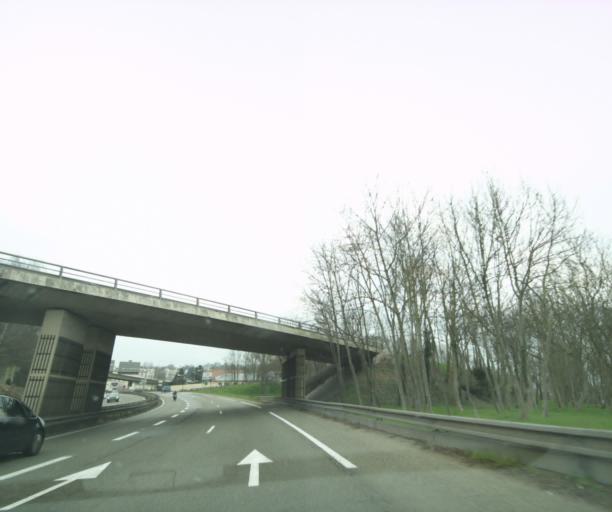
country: FR
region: Ile-de-France
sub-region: Departement des Yvelines
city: Le Pecq
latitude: 48.8862
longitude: 2.1049
